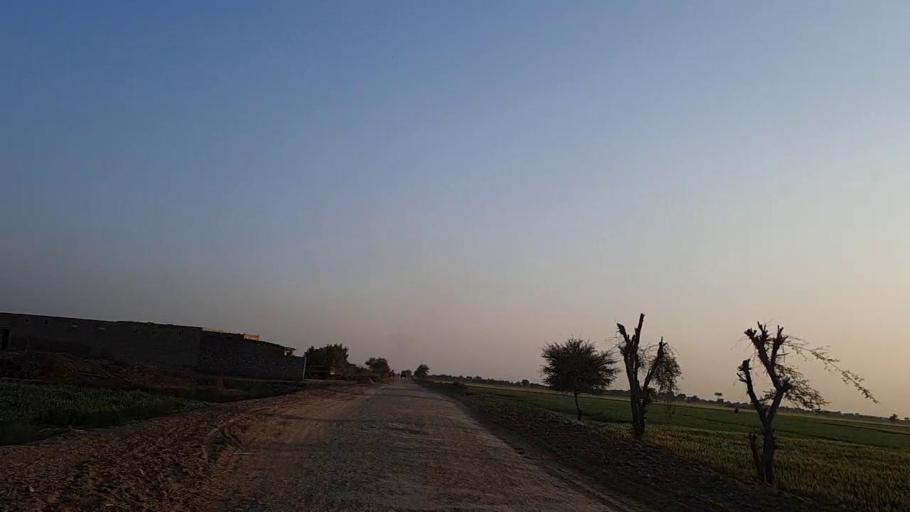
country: PK
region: Sindh
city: Shahdadpur
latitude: 25.9966
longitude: 68.4935
